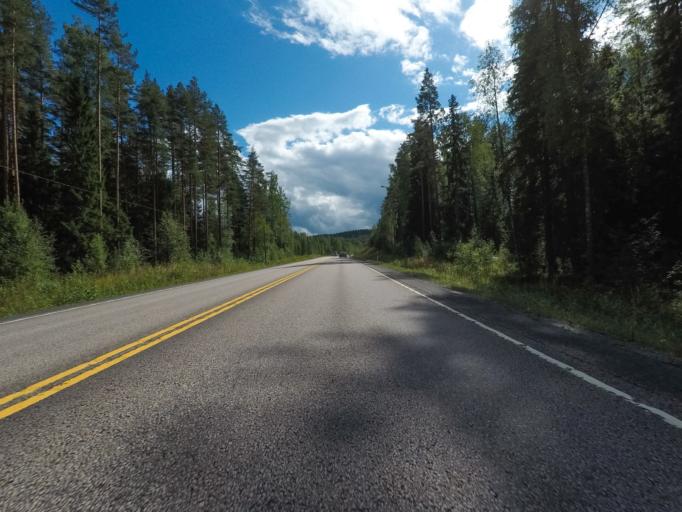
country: FI
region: Central Finland
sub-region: Jyvaeskylae
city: Toivakka
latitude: 62.0595
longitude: 26.0493
